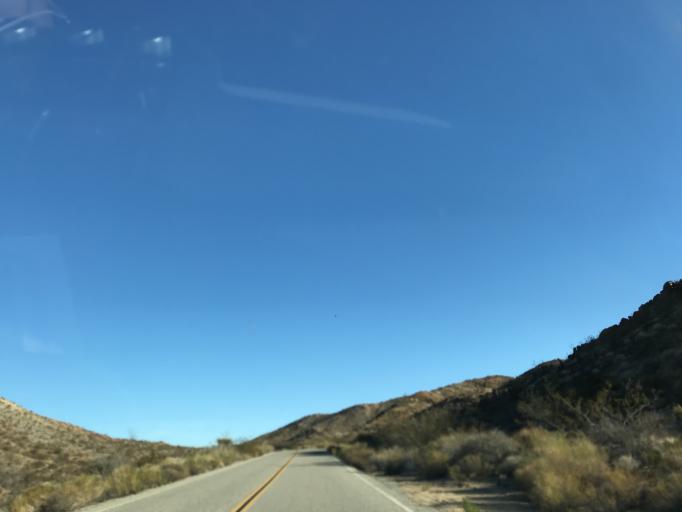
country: US
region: California
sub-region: Riverside County
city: Mecca
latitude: 33.7367
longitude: -115.8239
